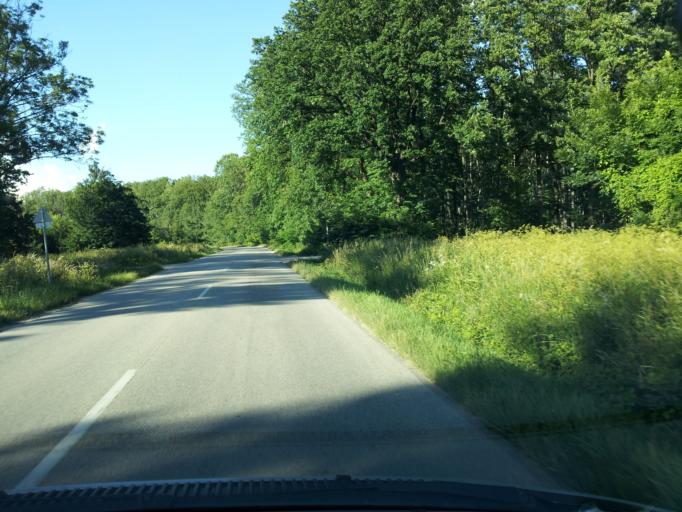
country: HU
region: Veszprem
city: Zirc
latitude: 47.2346
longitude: 17.8583
